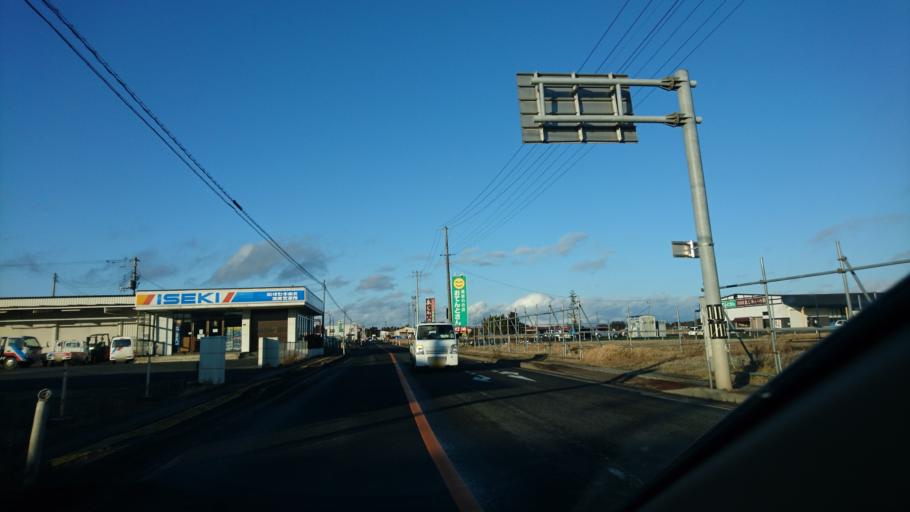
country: JP
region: Miyagi
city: Furukawa
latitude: 38.5772
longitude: 140.8601
